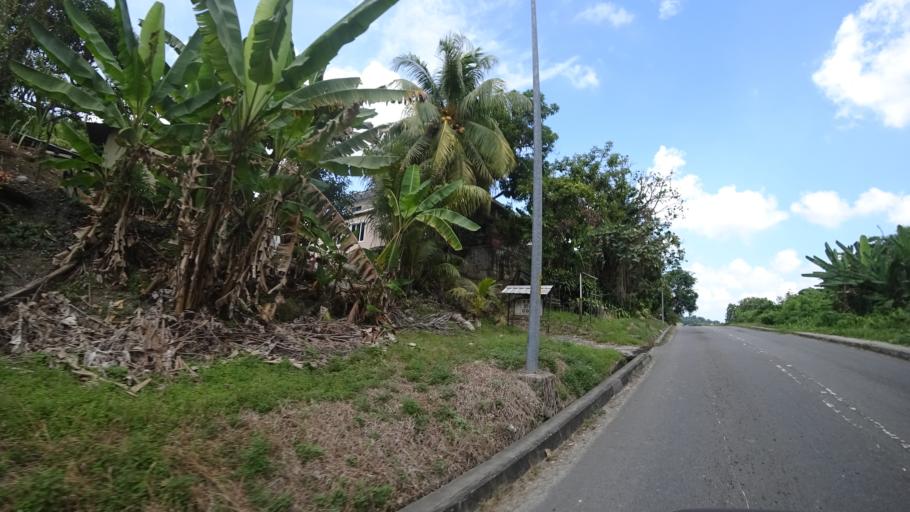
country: BN
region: Brunei and Muara
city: Bandar Seri Begawan
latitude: 4.8942
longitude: 114.9185
